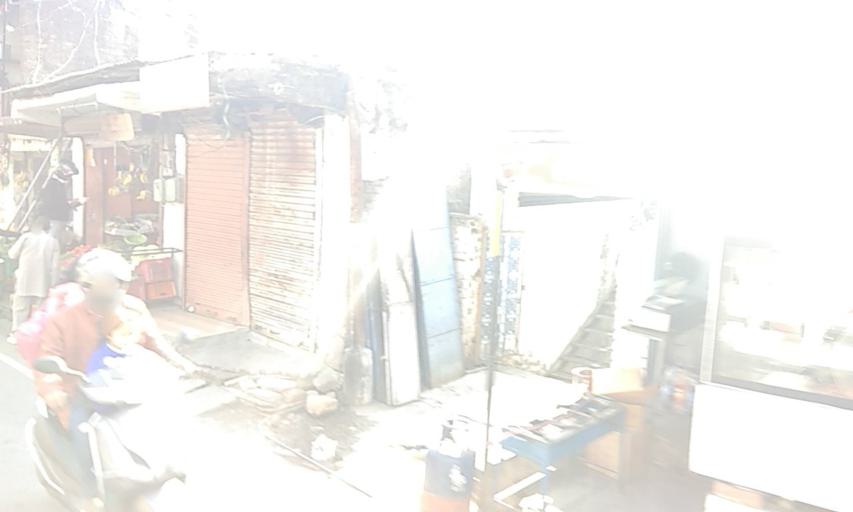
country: IN
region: Himachal Pradesh
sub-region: Kangra
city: Dharmsala
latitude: 32.1831
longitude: 76.3745
